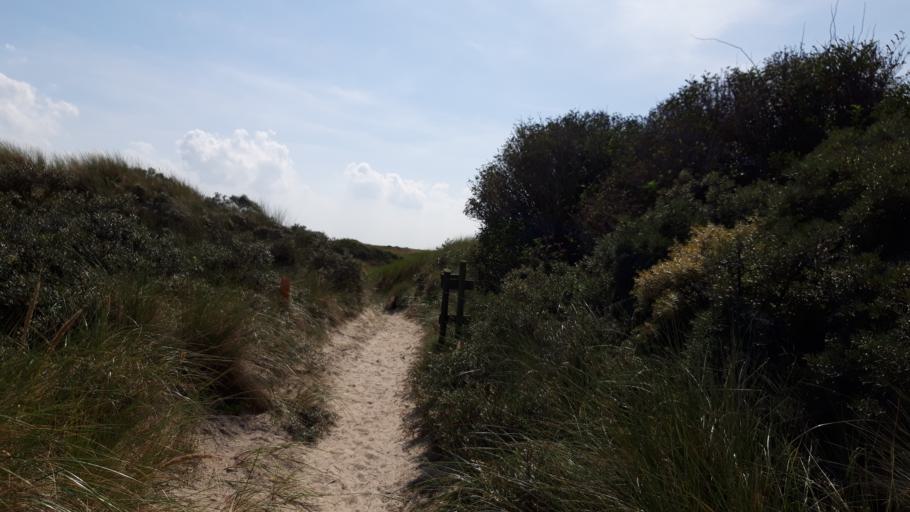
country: NL
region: Friesland
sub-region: Gemeente Ameland
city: Nes
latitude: 53.4631
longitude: 5.8646
